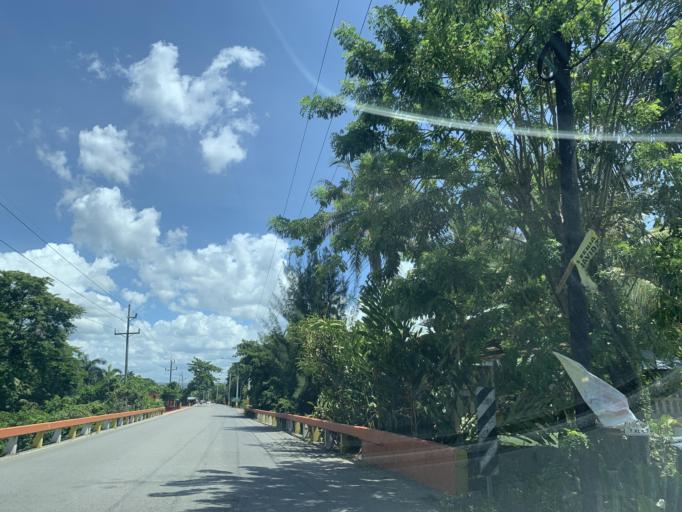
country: DO
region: Puerto Plata
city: Cabarete
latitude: 19.7057
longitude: -70.3840
